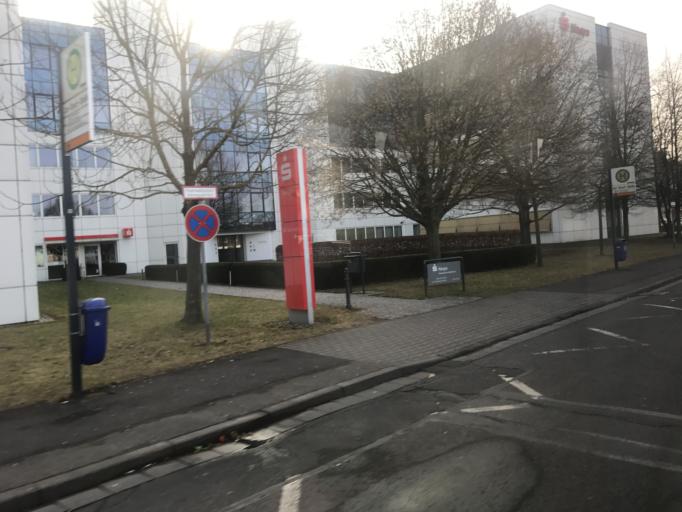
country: DE
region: Hesse
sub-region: Regierungsbezirk Darmstadt
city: Wiesbaden
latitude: 50.0428
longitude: 8.2192
